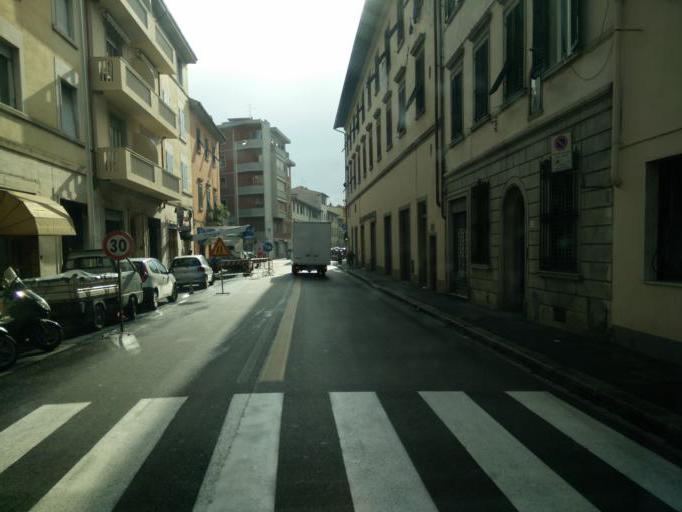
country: IT
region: Tuscany
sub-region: Province of Florence
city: Florence
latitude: 43.7822
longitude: 11.2352
